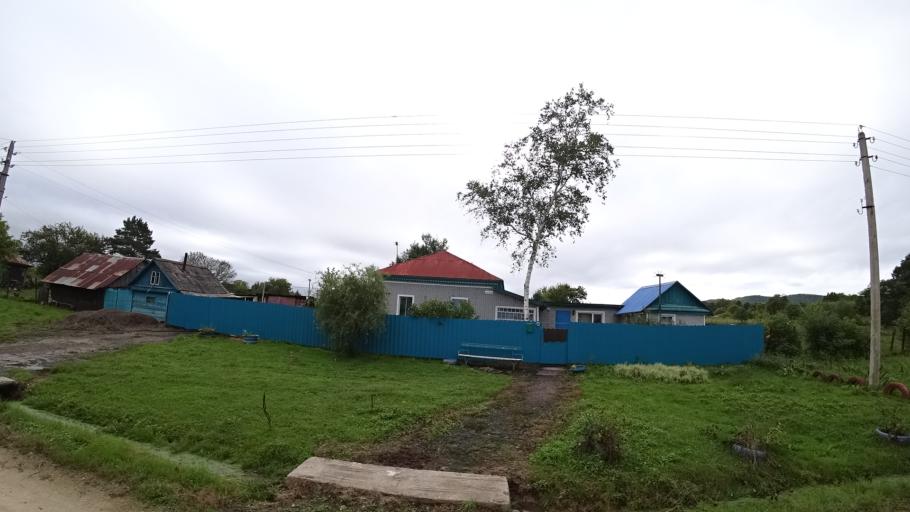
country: RU
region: Primorskiy
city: Rettikhovka
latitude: 44.1363
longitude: 132.6433
